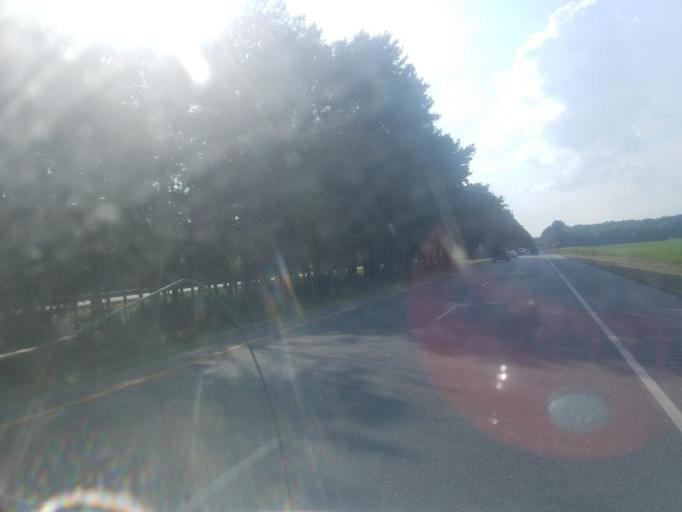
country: US
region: Maryland
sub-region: Worcester County
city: Berlin
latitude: 38.3723
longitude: -75.2766
